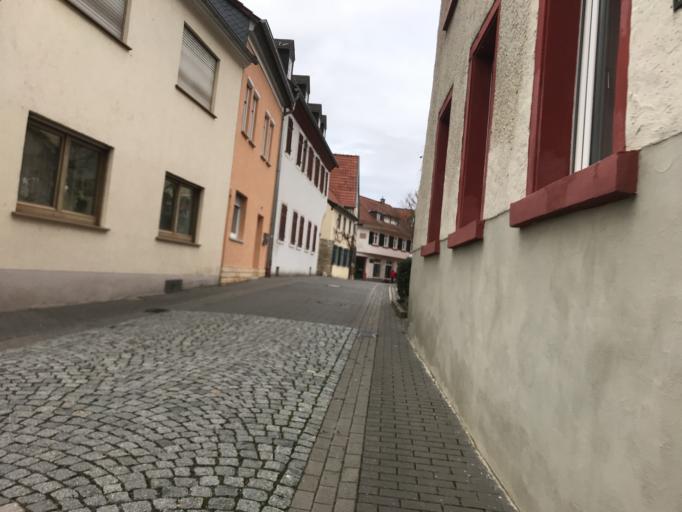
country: DE
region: Rheinland-Pfalz
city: Ingelheim am Rhein
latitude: 49.9630
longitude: 8.0601
